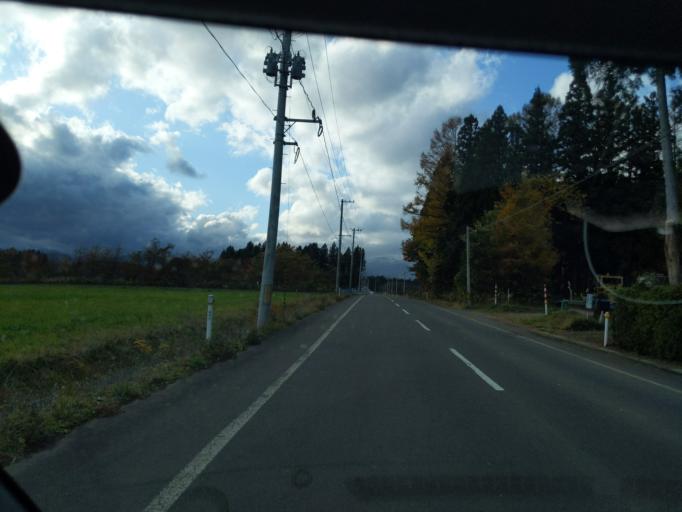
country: JP
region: Iwate
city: Mizusawa
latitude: 39.1104
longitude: 140.9968
